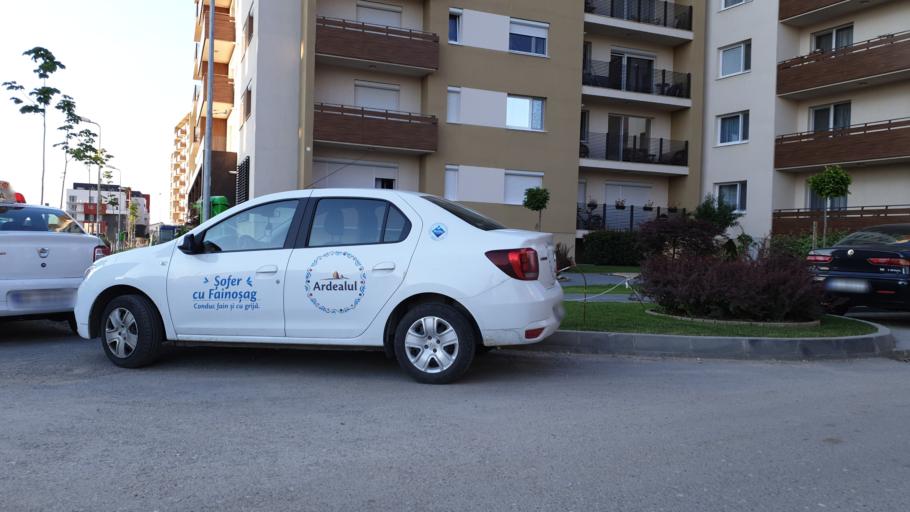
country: RO
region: Brasov
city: Brasov
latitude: 45.6726
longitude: 25.6089
